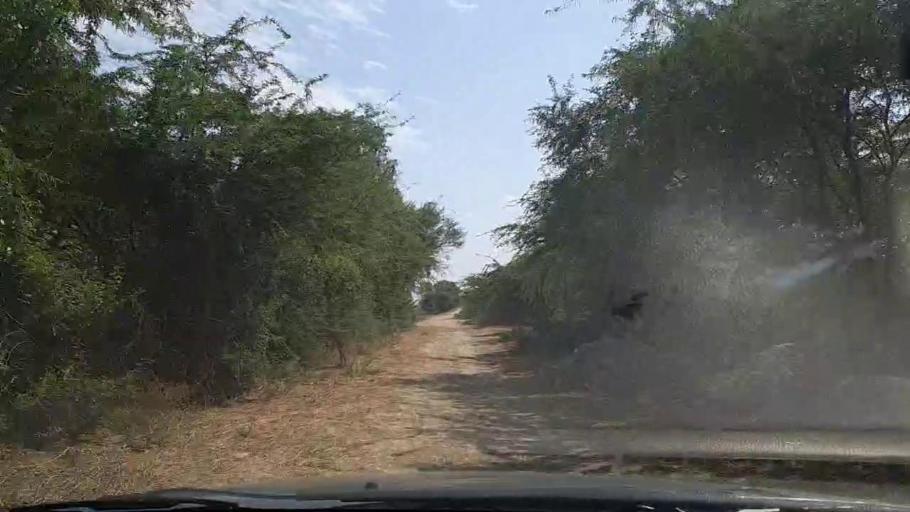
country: PK
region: Sindh
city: Mirpur Batoro
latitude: 24.5596
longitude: 68.2013
